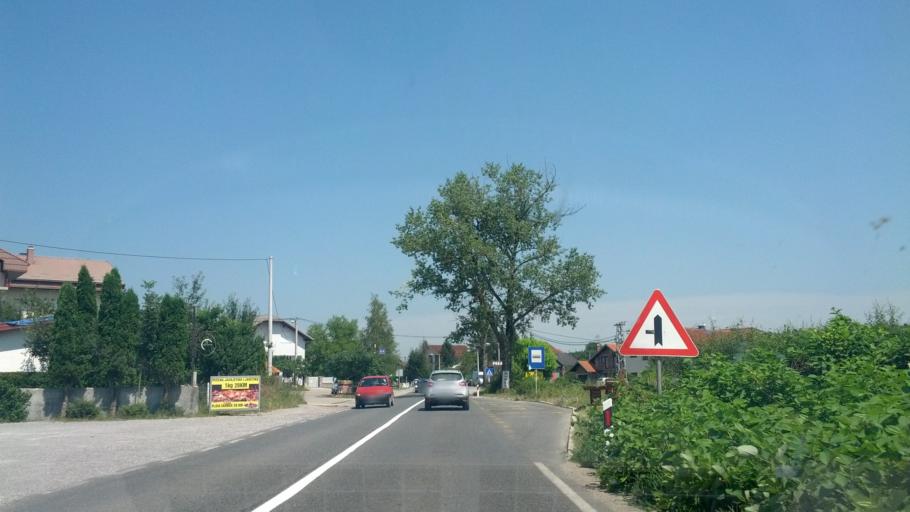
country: BA
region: Federation of Bosnia and Herzegovina
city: Bihac
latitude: 44.8360
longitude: 15.8317
